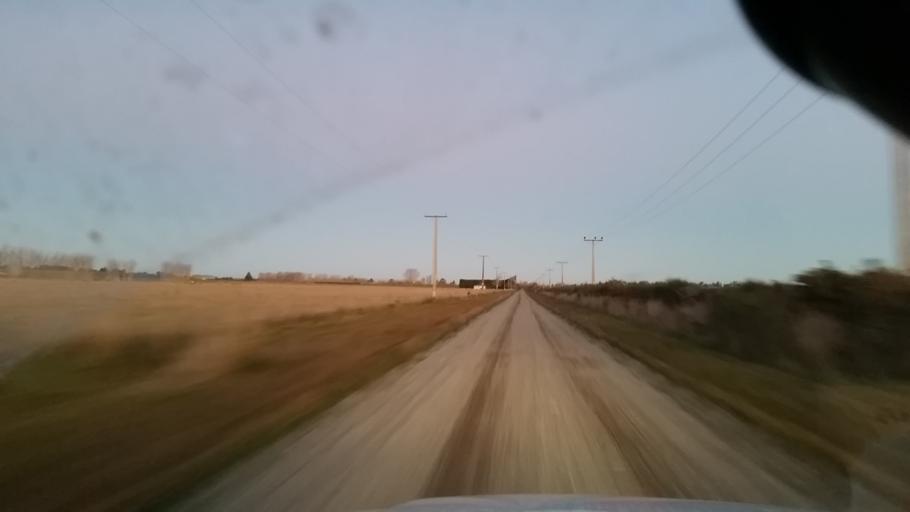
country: NZ
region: Canterbury
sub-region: Ashburton District
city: Tinwald
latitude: -43.9928
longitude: 171.6596
